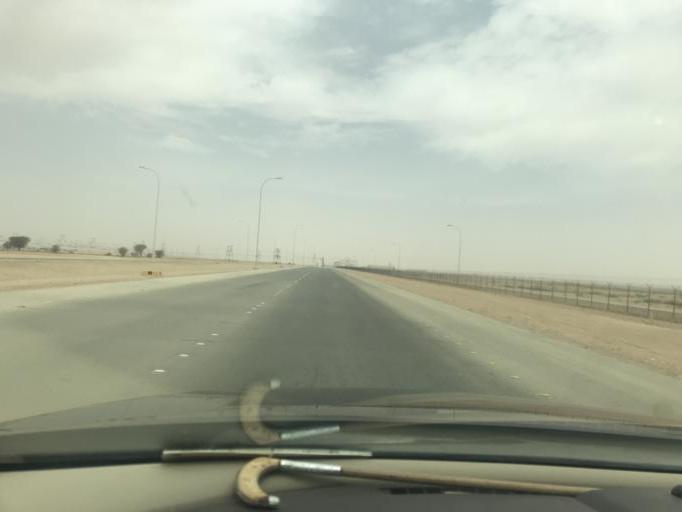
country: SA
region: Ar Riyad
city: Riyadh
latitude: 24.9660
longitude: 46.6661
